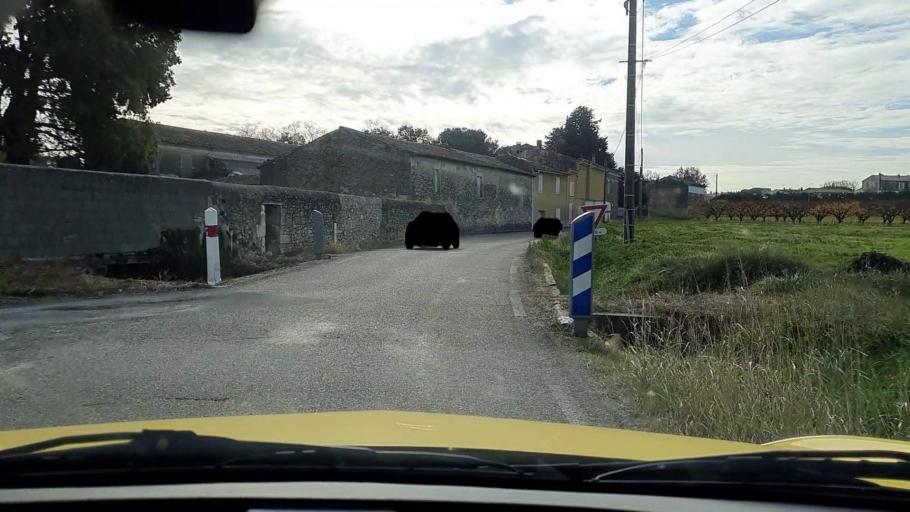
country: FR
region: Languedoc-Roussillon
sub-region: Departement du Gard
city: Jonquieres-Saint-Vincent
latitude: 43.8316
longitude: 4.5649
